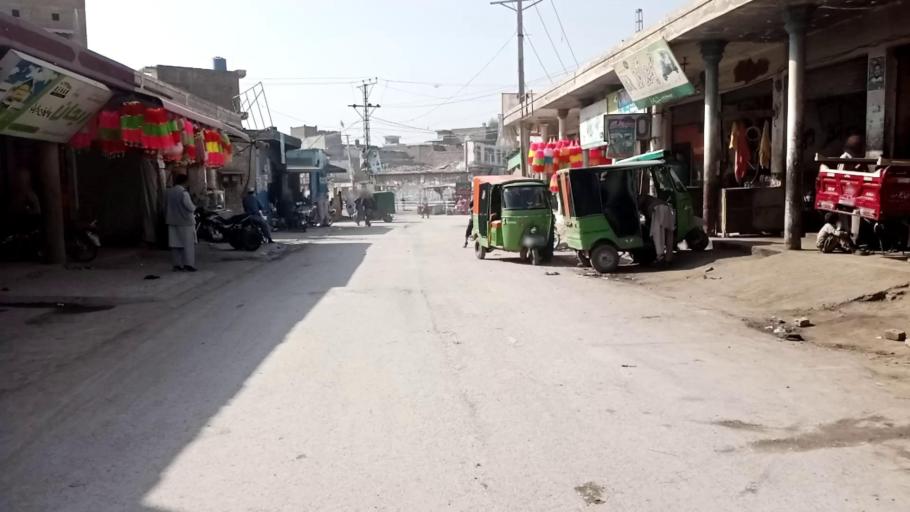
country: PK
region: Khyber Pakhtunkhwa
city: Peshawar
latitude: 33.9927
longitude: 71.5840
